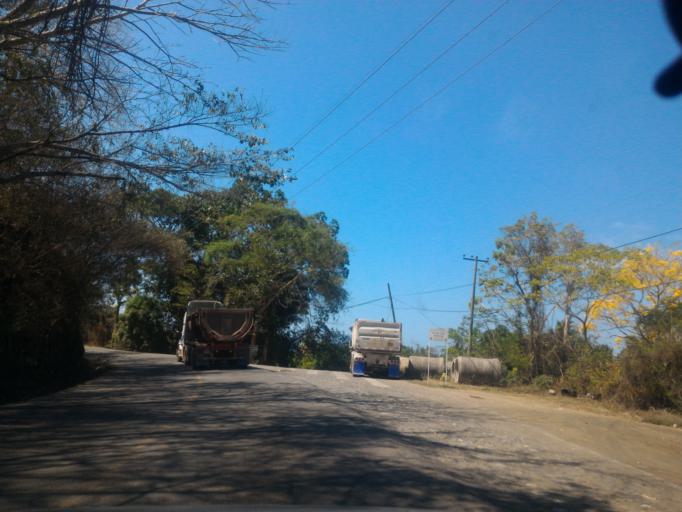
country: MX
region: Michoacan
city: Coahuayana Viejo
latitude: 18.6268
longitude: -103.6713
